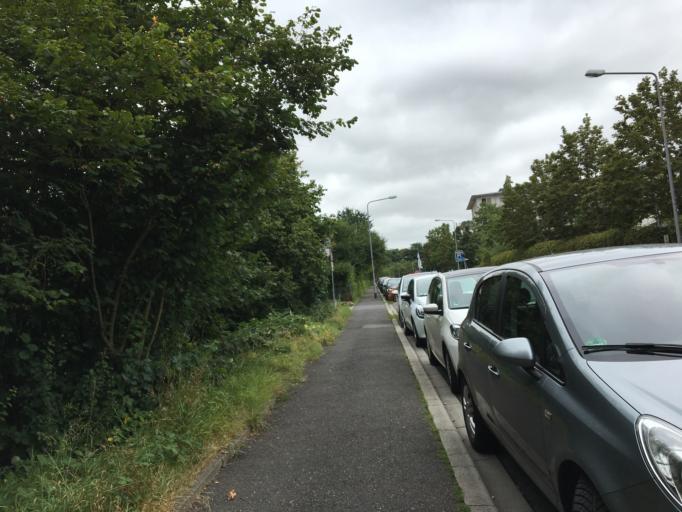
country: DE
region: Hesse
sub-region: Regierungsbezirk Darmstadt
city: Wiesbaden
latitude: 50.0875
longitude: 8.2723
